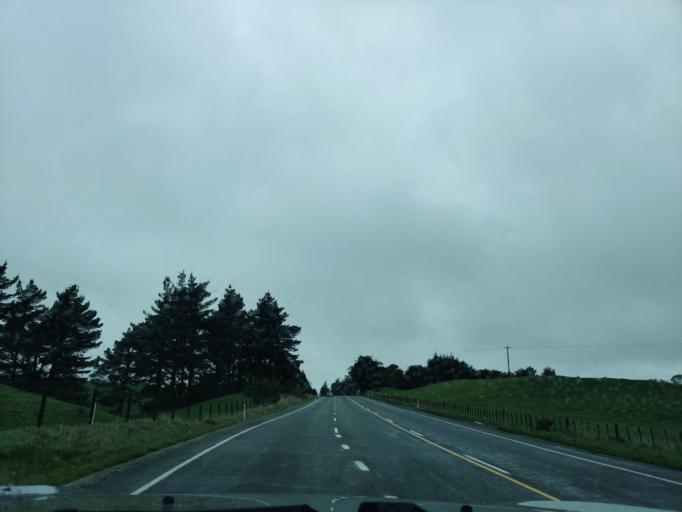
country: NZ
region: Manawatu-Wanganui
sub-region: Palmerston North City
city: Palmerston North
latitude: -40.0814
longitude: 176.1975
